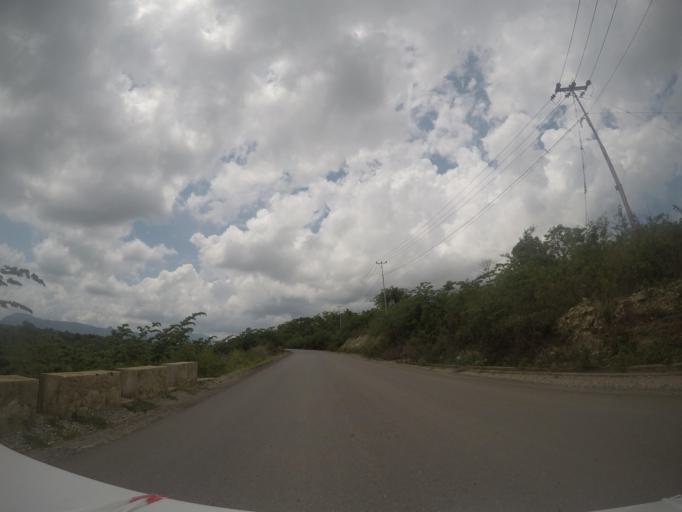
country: TL
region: Baucau
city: Venilale
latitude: -8.5567
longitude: 126.4035
